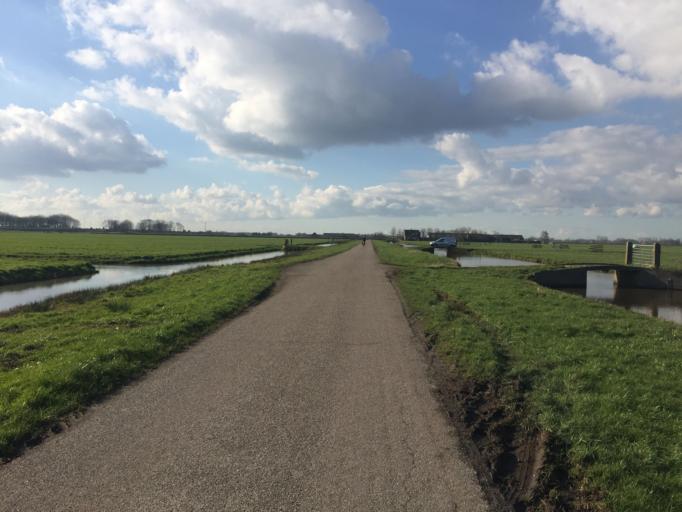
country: NL
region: Utrecht
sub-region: Gemeente Oudewater
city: Oudewater
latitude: 52.0665
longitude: 4.8169
